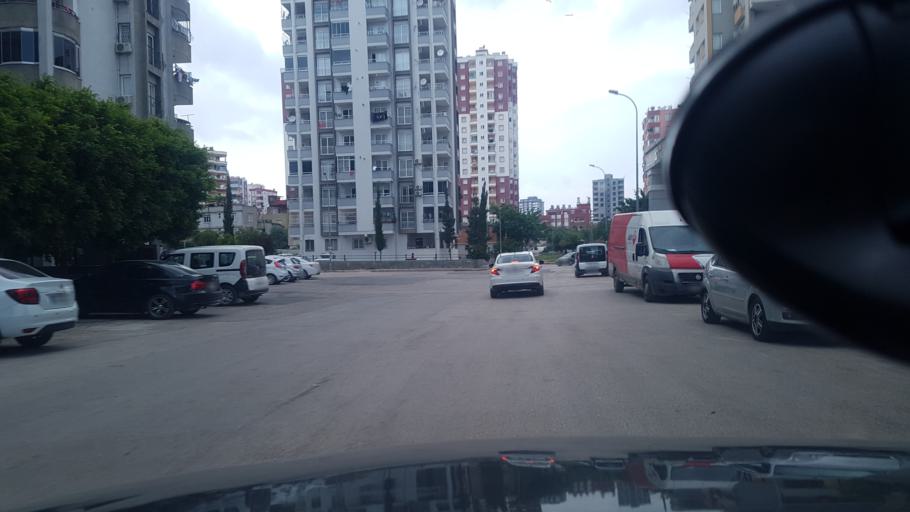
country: TR
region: Adana
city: Seyhan
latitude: 37.0265
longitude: 35.2882
